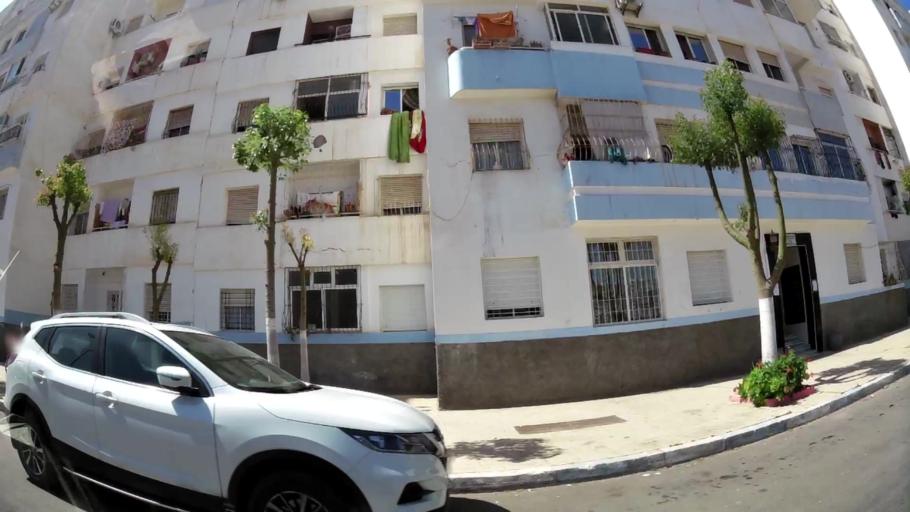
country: MA
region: Oued ed Dahab-Lagouira
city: Dakhla
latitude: 30.4317
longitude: -9.5633
